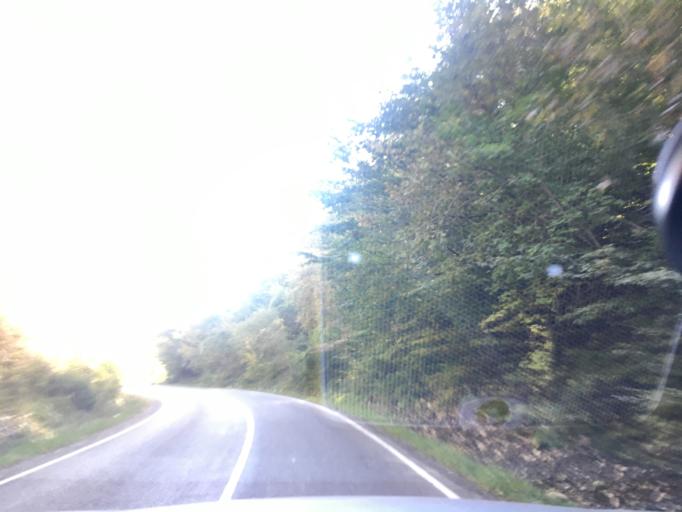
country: GE
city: Didi Lilo
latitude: 41.8790
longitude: 44.9214
